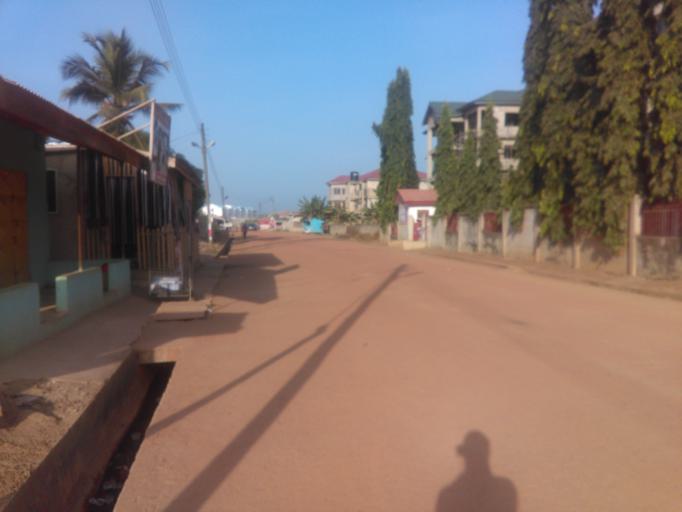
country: GH
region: Central
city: Cape Coast
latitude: 5.1098
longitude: -1.2961
